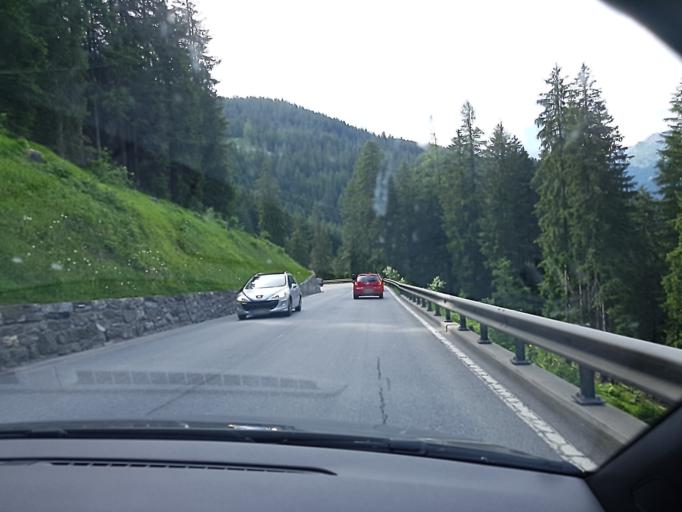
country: CH
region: Grisons
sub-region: Praettigau/Davos District
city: Klosters Serneus
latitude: 46.8516
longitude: 9.8819
